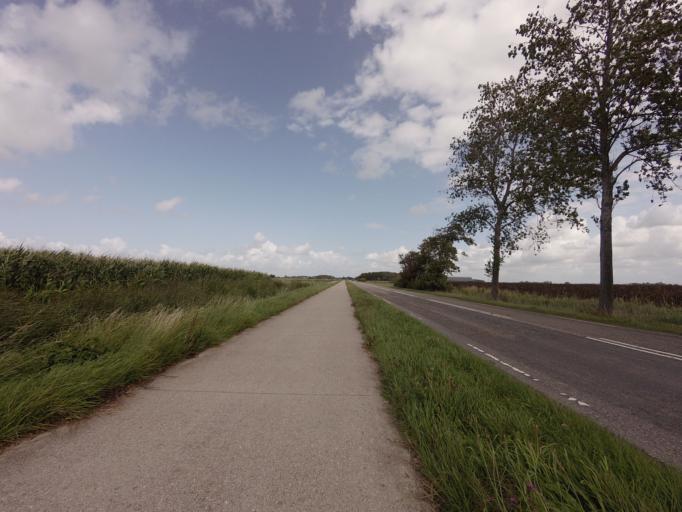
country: NL
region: Friesland
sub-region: Gemeente Harlingen
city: Harlingen
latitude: 53.1356
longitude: 5.4717
